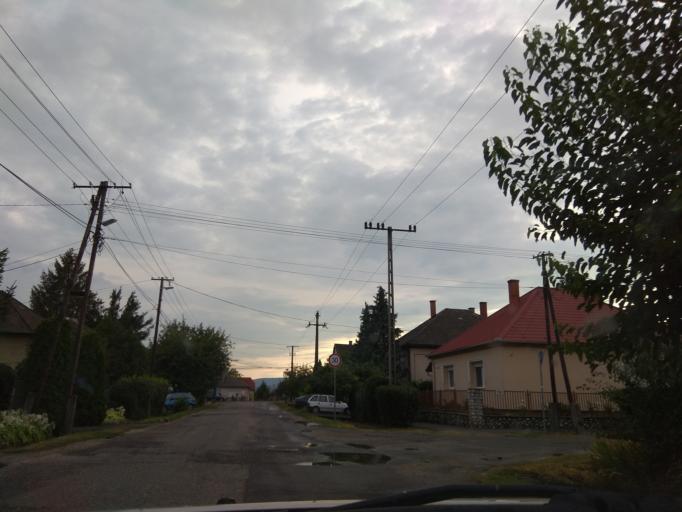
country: HU
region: Borsod-Abauj-Zemplen
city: Felsozsolca
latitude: 48.0741
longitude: 20.8281
